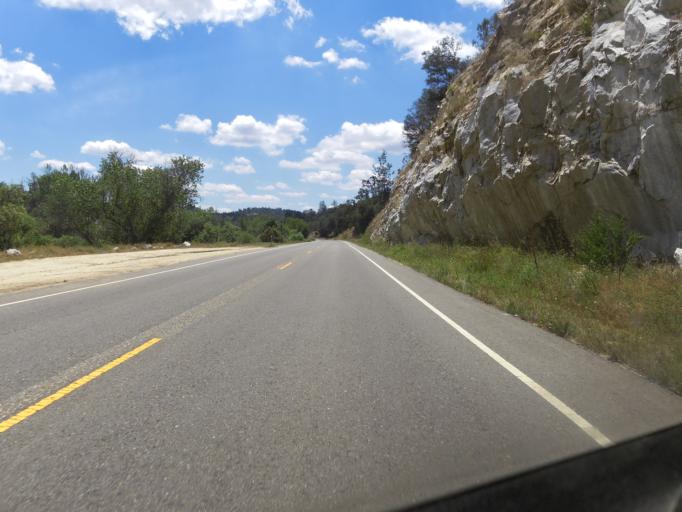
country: US
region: California
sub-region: Madera County
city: Coarsegold
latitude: 37.1693
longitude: -119.6373
